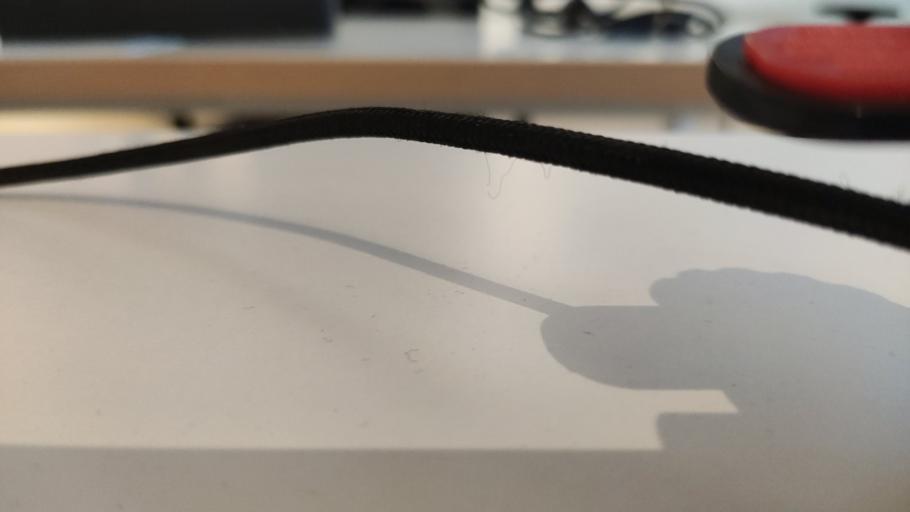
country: RU
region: Moskovskaya
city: Sychevo
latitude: 55.8476
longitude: 36.3484
